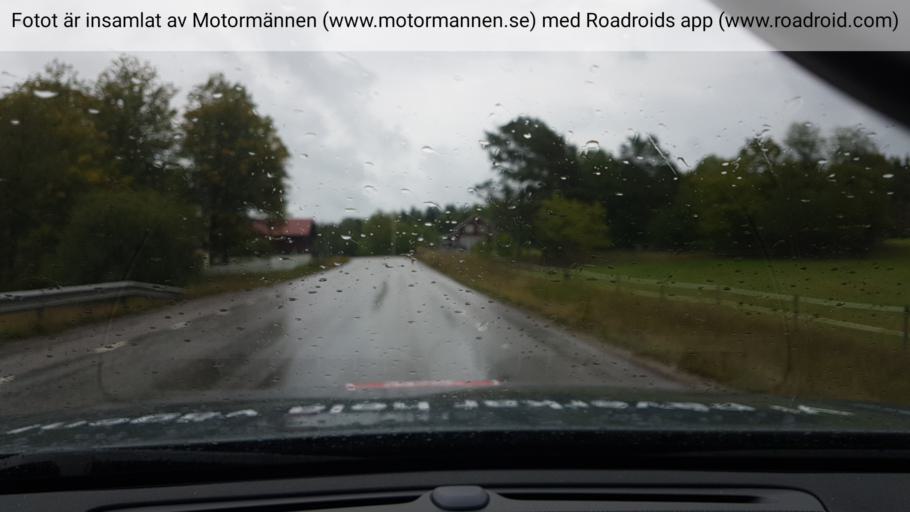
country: SE
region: Stockholm
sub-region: Haninge Kommun
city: Jordbro
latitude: 59.0589
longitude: 18.0424
